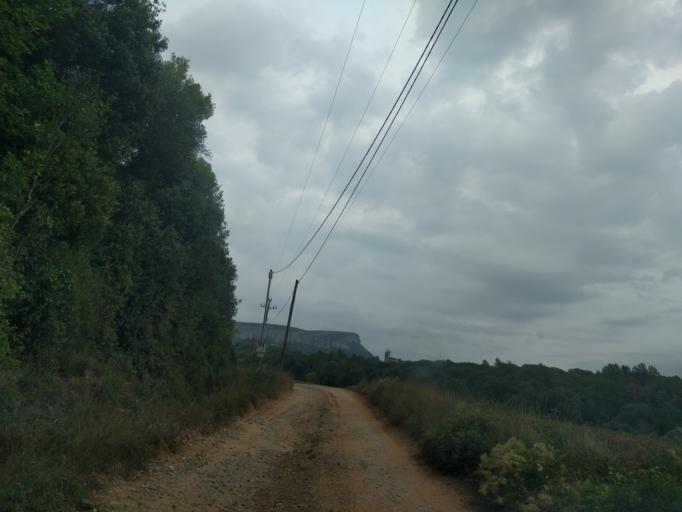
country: ES
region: Catalonia
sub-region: Provincia de Girona
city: la Cellera de Ter
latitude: 42.0021
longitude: 2.6312
